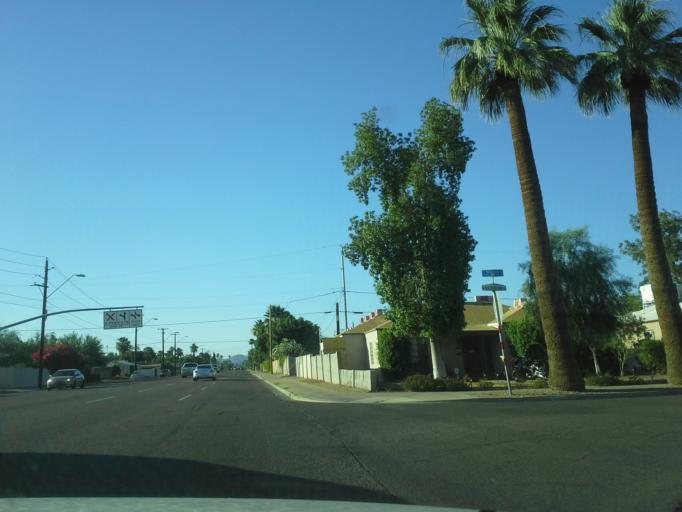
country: US
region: Arizona
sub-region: Maricopa County
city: Phoenix
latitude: 33.4738
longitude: -112.0828
